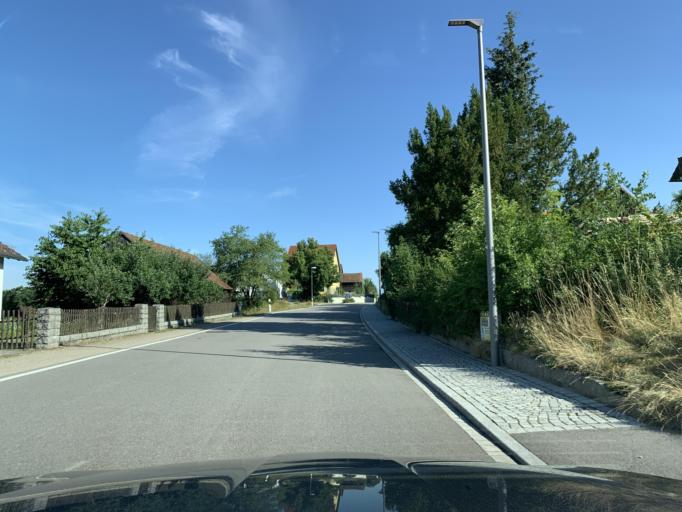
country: DE
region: Bavaria
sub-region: Upper Palatinate
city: Schwarzhofen
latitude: 49.3743
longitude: 12.3463
